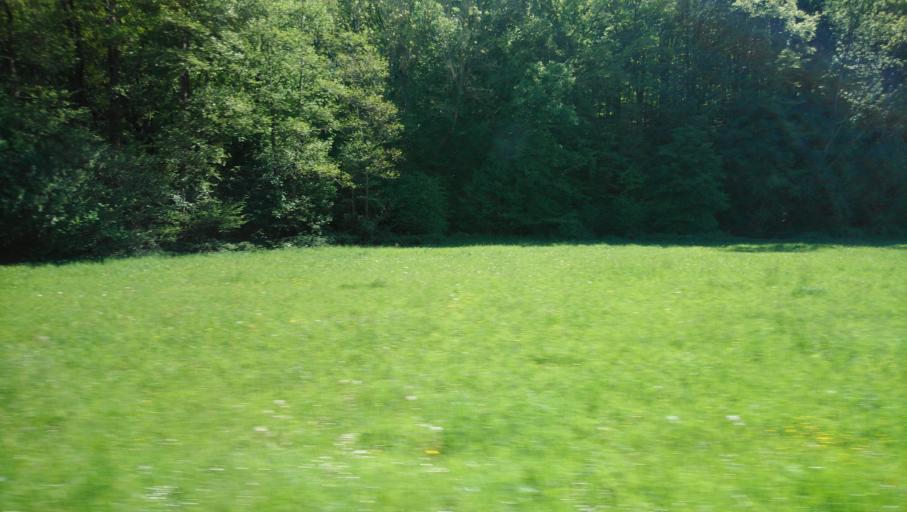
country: LU
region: Diekirch
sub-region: Canton de Vianden
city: Tandel
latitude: 49.8871
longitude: 6.1820
